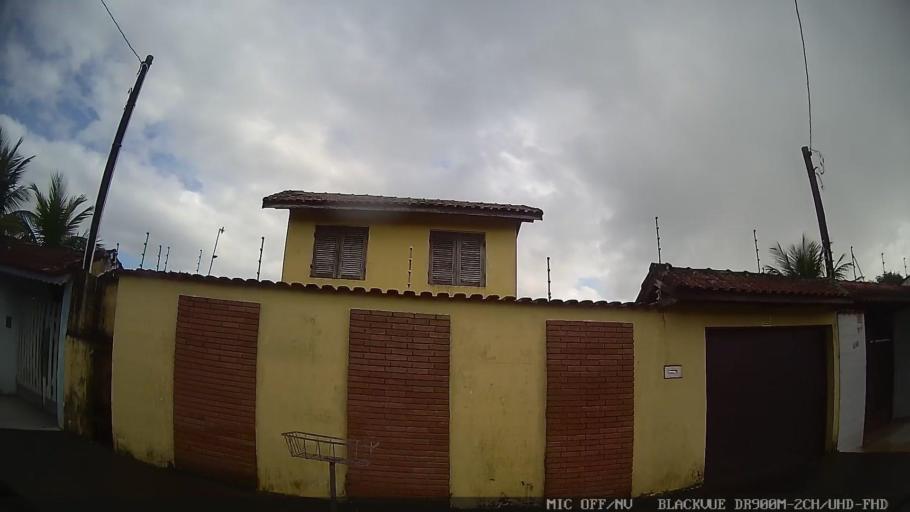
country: BR
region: Sao Paulo
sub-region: Itanhaem
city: Itanhaem
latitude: -24.2031
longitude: -46.8384
